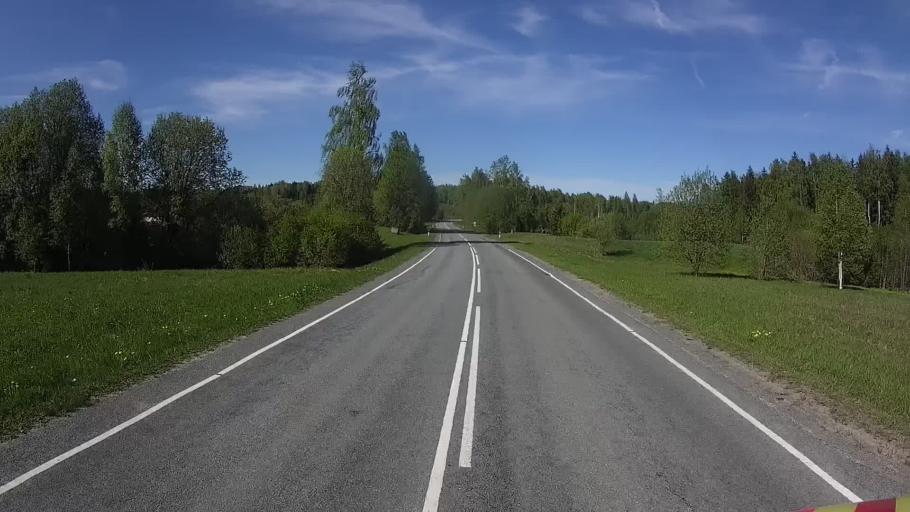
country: EE
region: Vorumaa
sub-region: Antsla vald
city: Vana-Antsla
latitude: 57.9590
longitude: 26.4521
